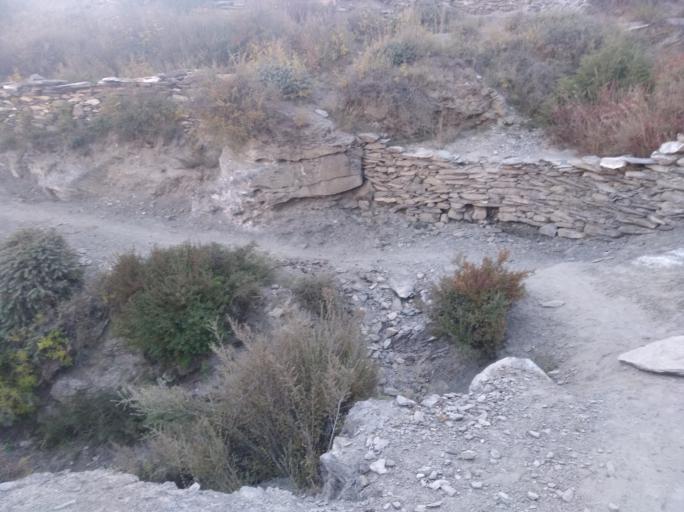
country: NP
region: Western Region
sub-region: Dhawalagiri Zone
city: Jomsom
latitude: 28.8816
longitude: 83.3522
